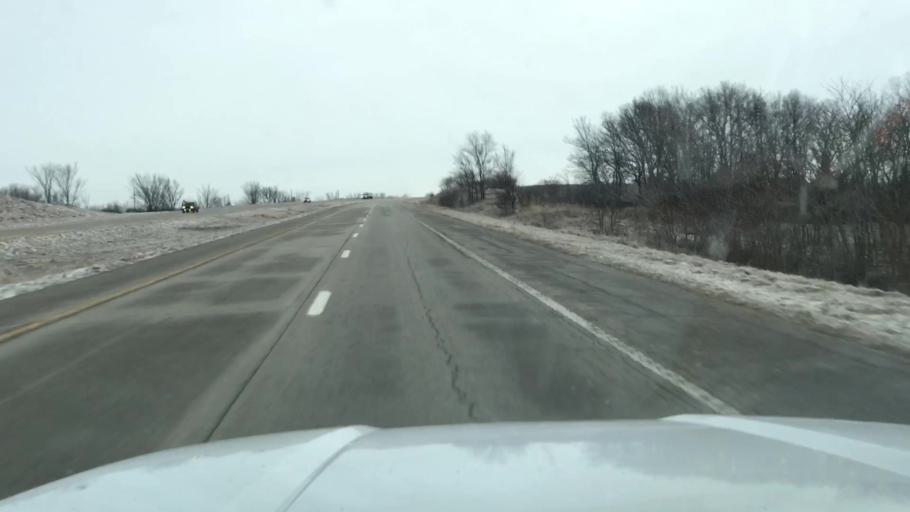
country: US
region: Missouri
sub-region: Andrew County
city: Savannah
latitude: 39.9088
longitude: -94.8592
